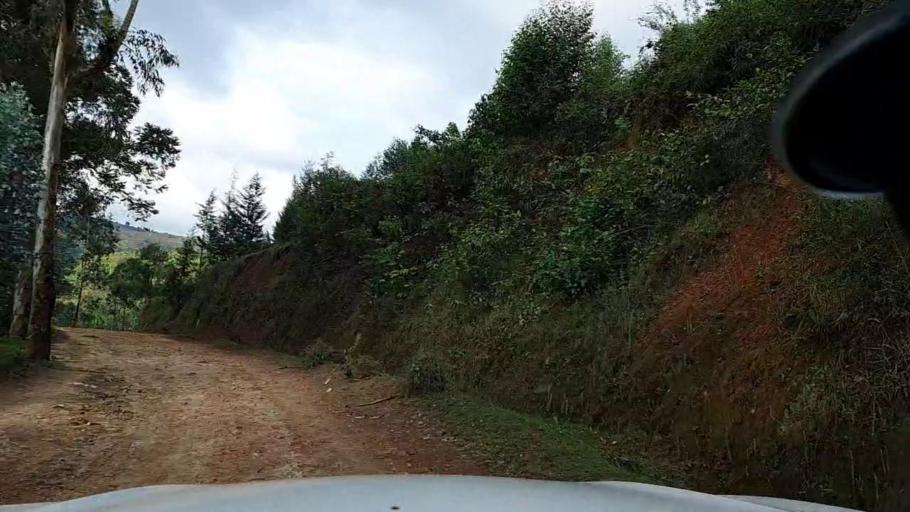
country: RW
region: Southern Province
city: Gitarama
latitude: -2.1635
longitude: 29.5514
